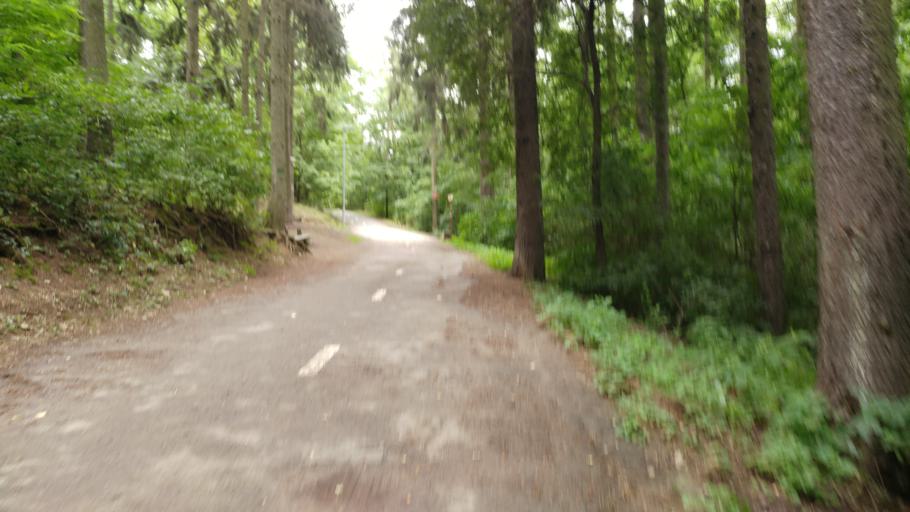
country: CZ
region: Central Bohemia
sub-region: Okres Praha-Zapad
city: Pruhonice
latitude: 50.0441
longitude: 14.5293
